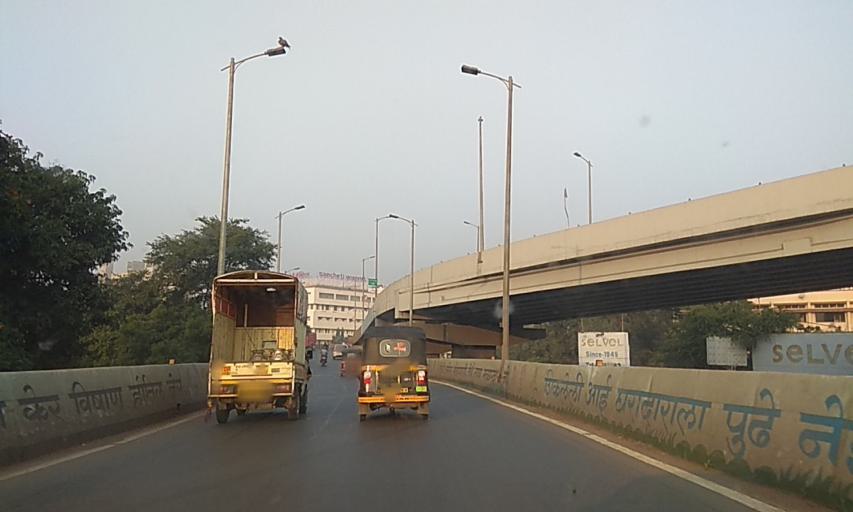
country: IN
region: Maharashtra
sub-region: Pune Division
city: Shivaji Nagar
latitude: 18.5301
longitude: 73.8552
